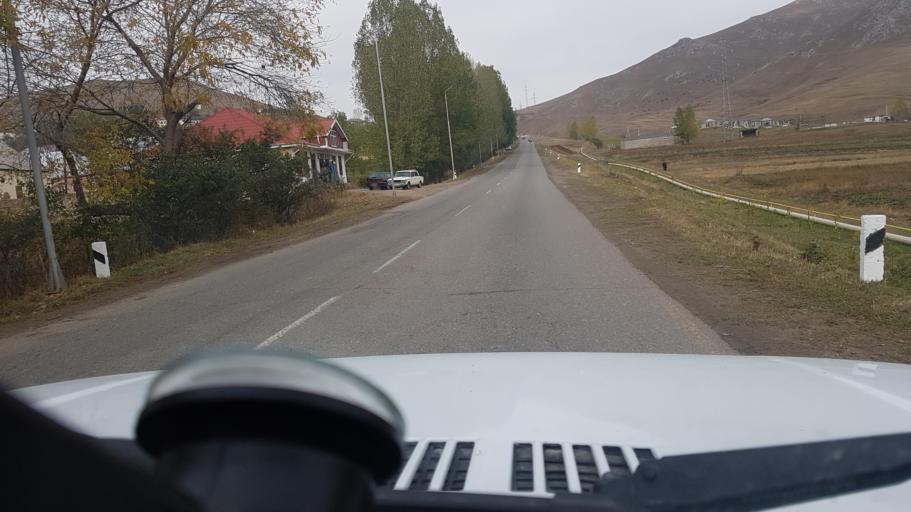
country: AZ
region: Gadabay Rayon
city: Ariqdam
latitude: 40.6077
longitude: 45.8125
